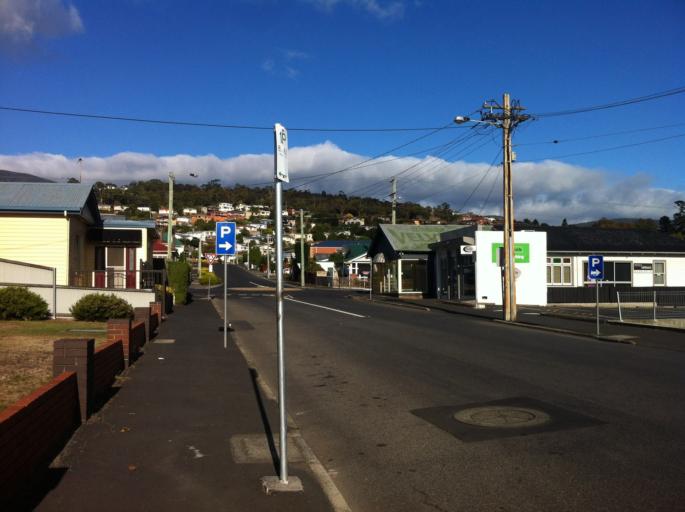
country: AU
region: Tasmania
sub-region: Glenorchy
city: Moonah
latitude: -42.8482
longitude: 147.2949
